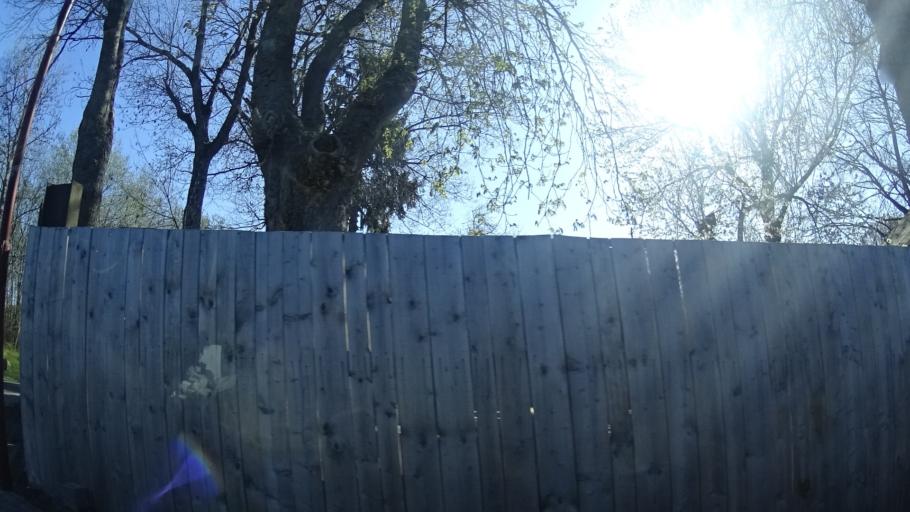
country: DE
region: Thuringia
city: Bohlen
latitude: 50.5880
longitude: 11.0401
